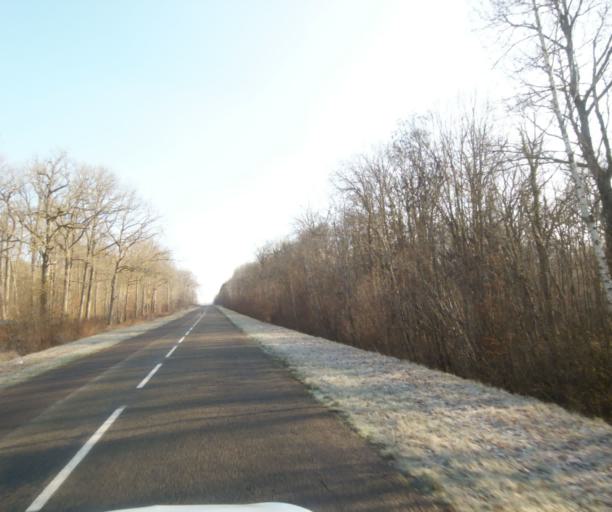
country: FR
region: Champagne-Ardenne
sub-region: Departement de la Haute-Marne
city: Montier-en-Der
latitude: 48.4828
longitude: 4.8124
